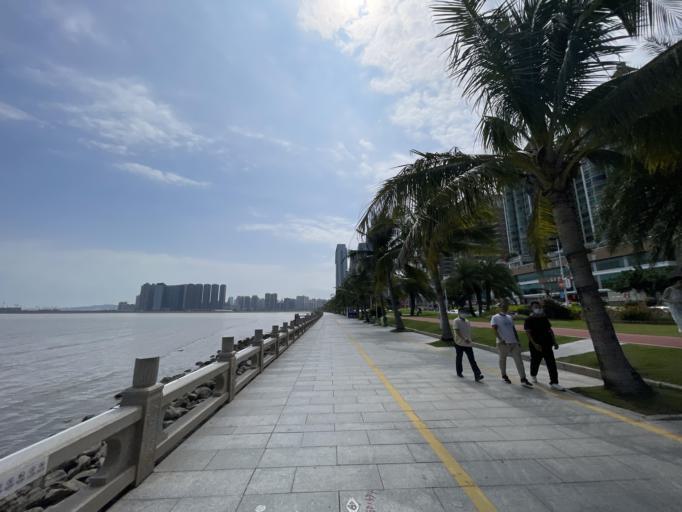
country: CN
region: Guangdong
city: Jida
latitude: 22.2284
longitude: 113.5584
